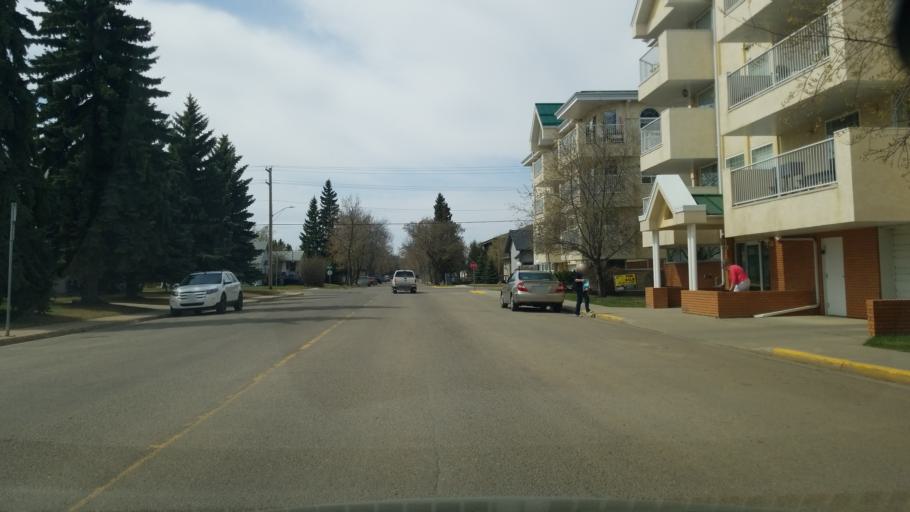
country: CA
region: Saskatchewan
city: Lloydminster
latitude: 53.2825
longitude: -110.0093
